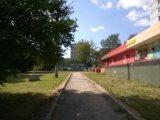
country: RU
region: Moskovskaya
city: Bol'shaya Setun'
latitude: 55.7466
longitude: 37.4094
